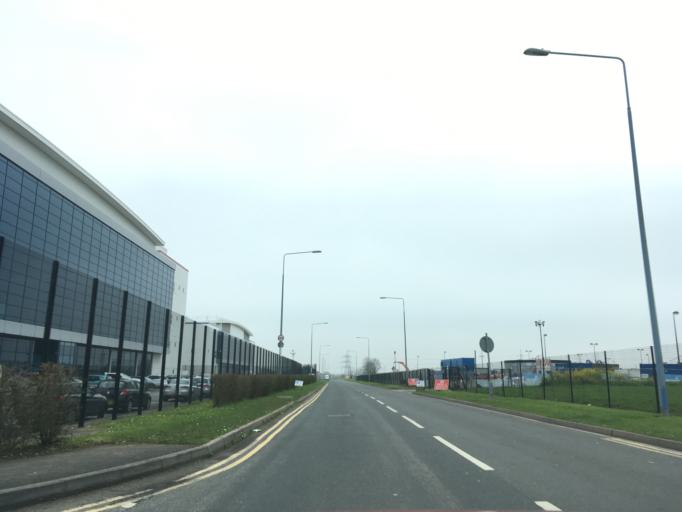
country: GB
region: Wales
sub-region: Newport
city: Marshfield
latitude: 51.5553
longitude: -3.0395
